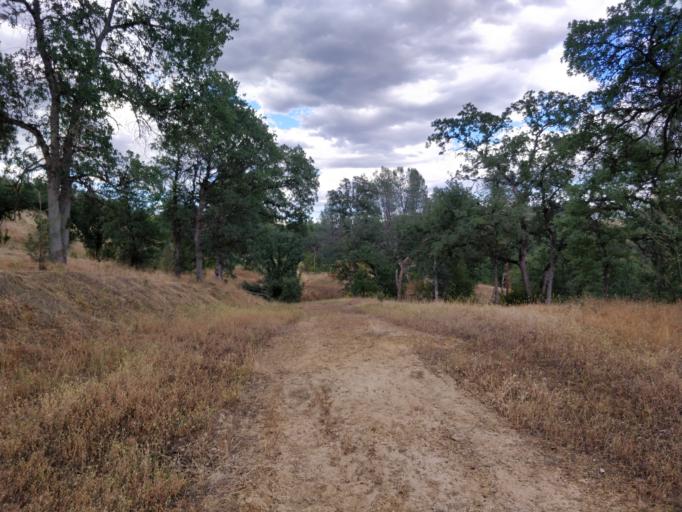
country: US
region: California
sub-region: Shasta County
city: Redding
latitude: 40.6098
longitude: -122.3846
